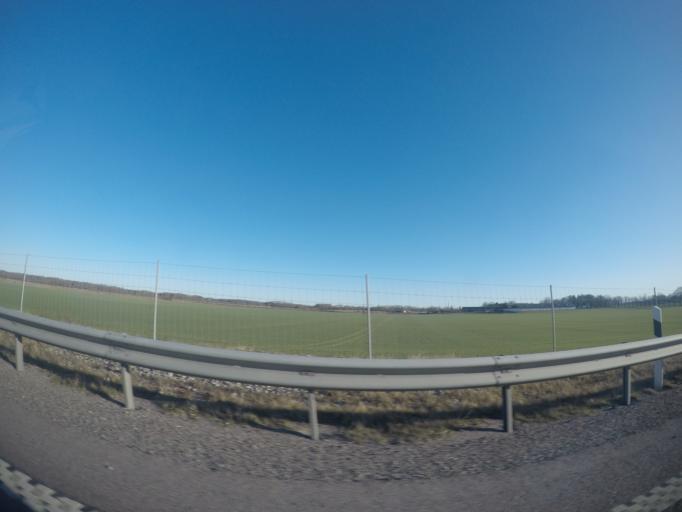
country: SE
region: Vaestmanland
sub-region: Kungsors Kommun
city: Kungsoer
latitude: 59.4098
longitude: 16.0060
